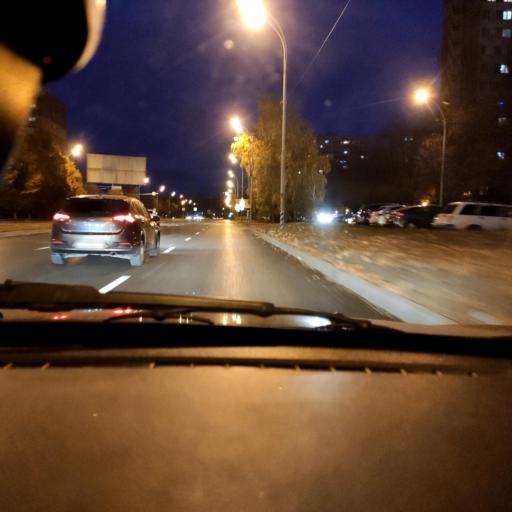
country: RU
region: Samara
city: Tol'yatti
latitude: 53.5130
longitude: 49.2989
